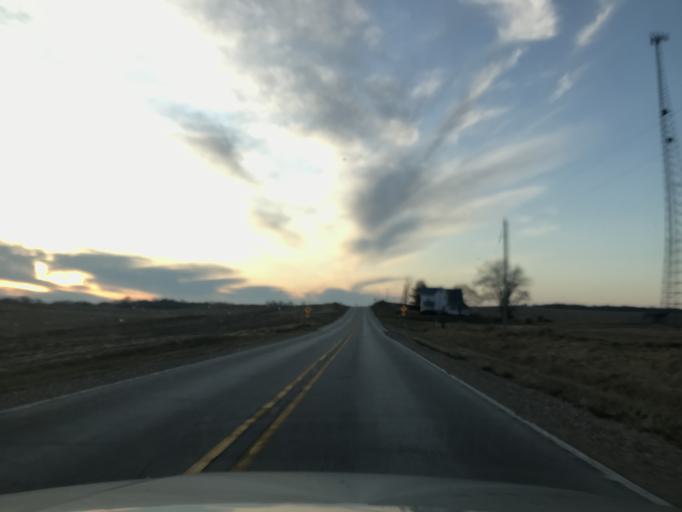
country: US
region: Illinois
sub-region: Henderson County
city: Oquawka
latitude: 41.0187
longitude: -90.8476
